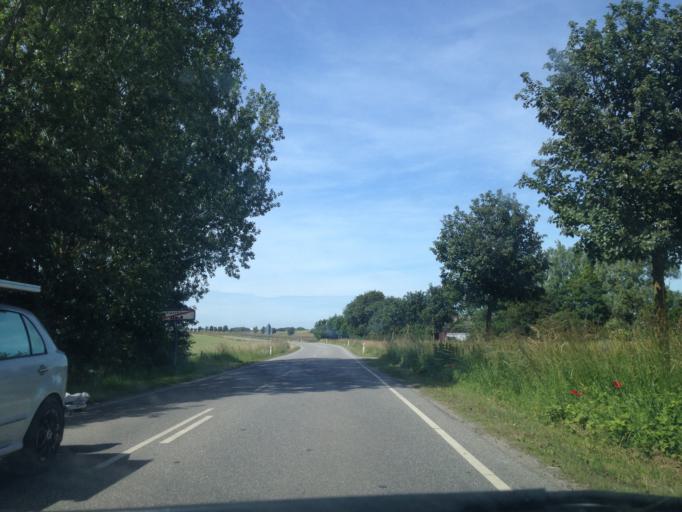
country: DK
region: Central Jutland
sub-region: Samso Kommune
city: Tranebjerg
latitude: 55.8367
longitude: 10.5826
